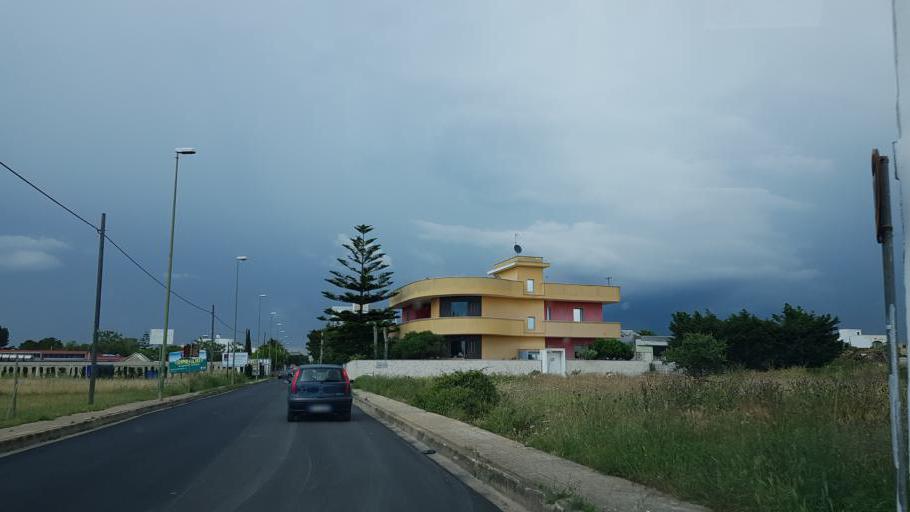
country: IT
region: Apulia
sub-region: Provincia di Lecce
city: Porto Cesareo
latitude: 40.2920
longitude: 17.8537
